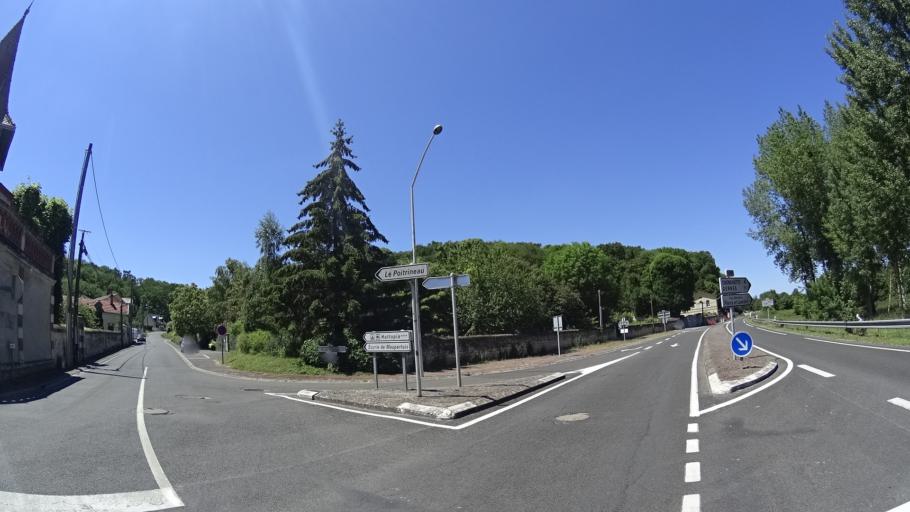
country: FR
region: Pays de la Loire
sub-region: Departement de Maine-et-Loire
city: Saumur
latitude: 47.2799
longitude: -0.1199
